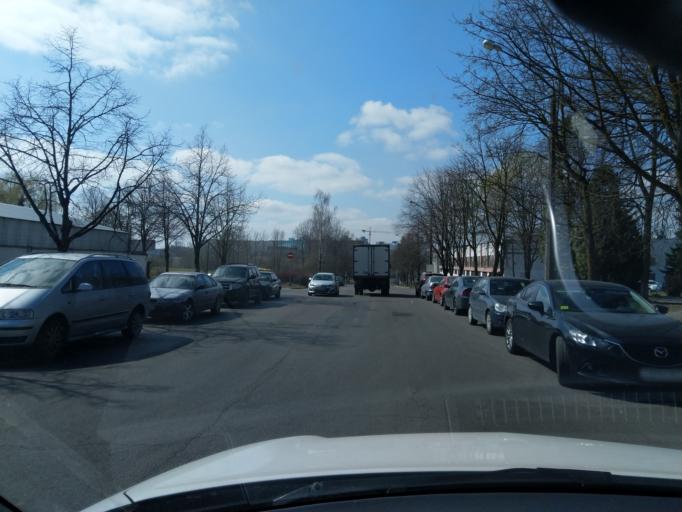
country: BY
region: Minsk
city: Syenitsa
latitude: 53.8649
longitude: 27.5050
